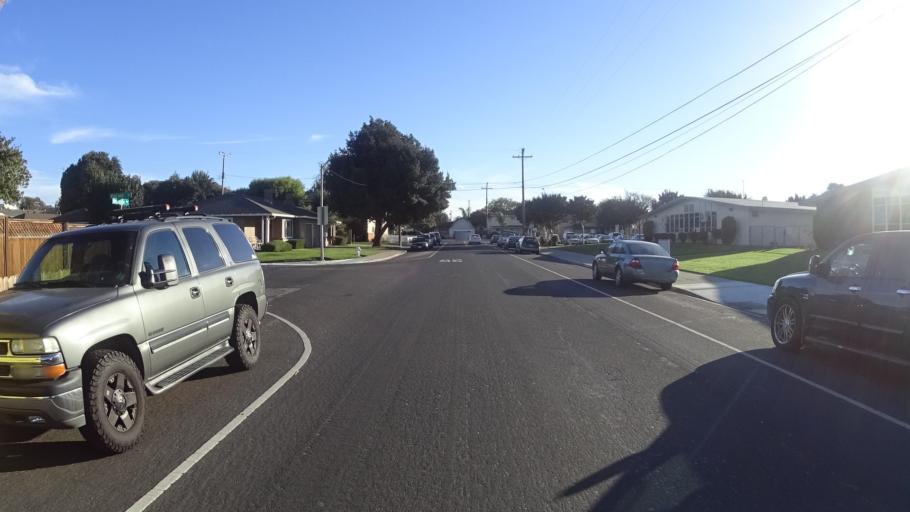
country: US
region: California
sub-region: Santa Clara County
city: Santa Clara
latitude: 37.3679
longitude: -121.9904
